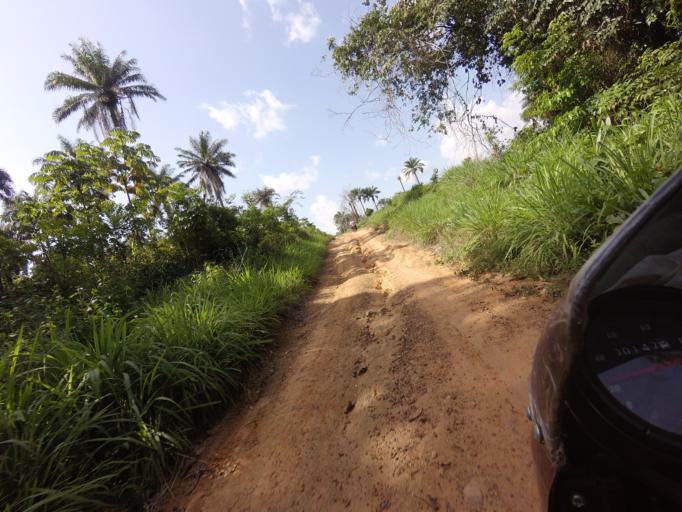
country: SL
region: Eastern Province
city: Kailahun
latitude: 8.3482
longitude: -10.7140
